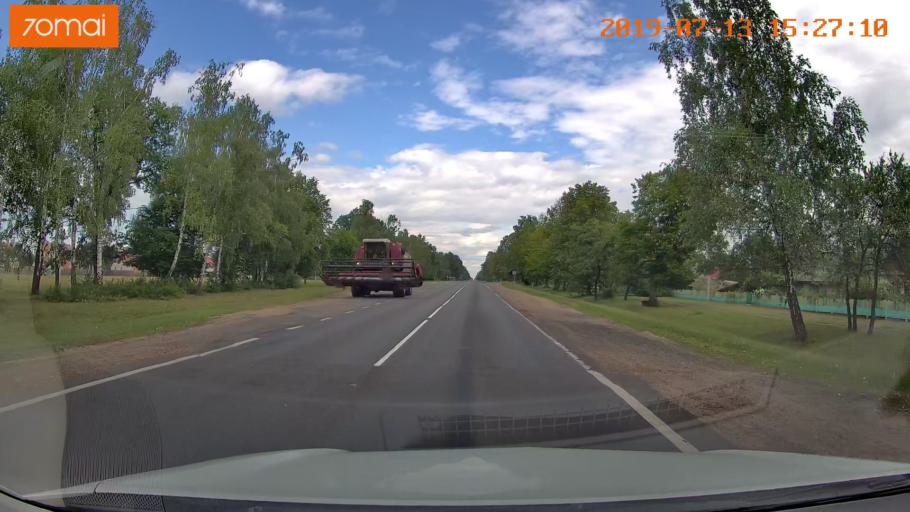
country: BY
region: Mogilev
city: Hlusha
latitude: 53.0990
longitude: 29.0147
